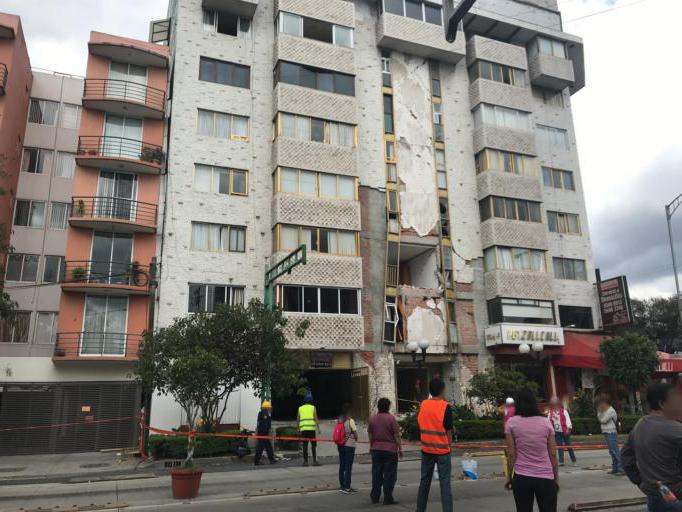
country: MX
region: Mexico City
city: Benito Juarez
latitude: 19.3951
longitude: -99.1451
